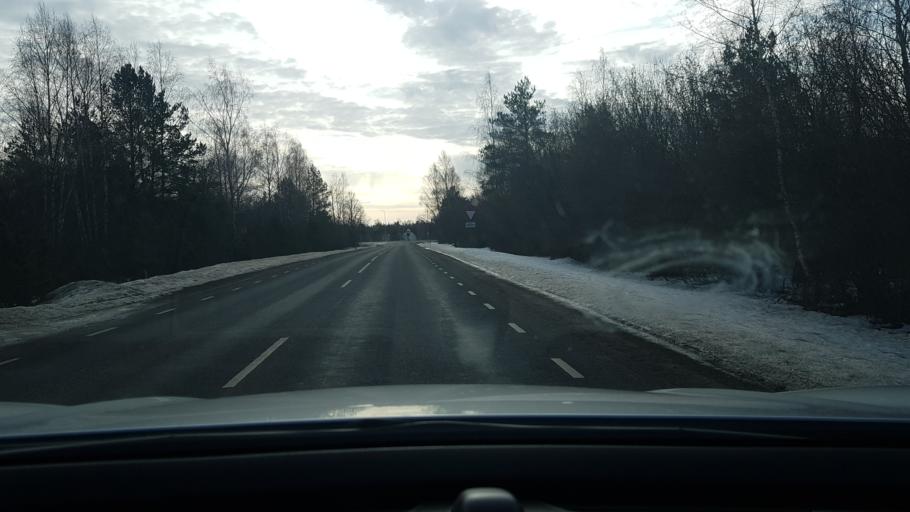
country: EE
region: Saare
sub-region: Kuressaare linn
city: Kuressaare
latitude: 58.2841
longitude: 22.5410
